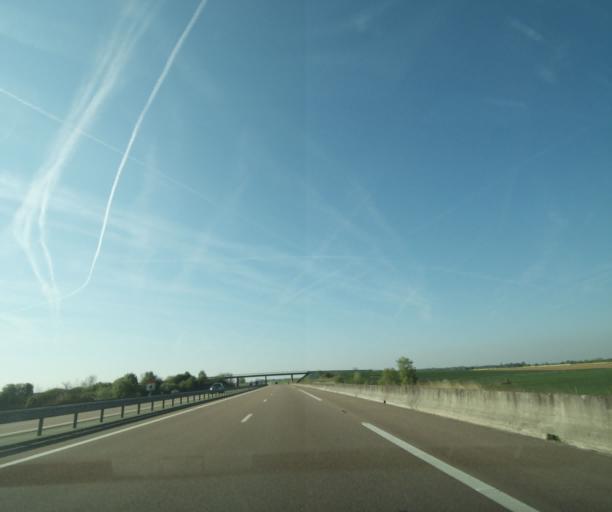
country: FR
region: Ile-de-France
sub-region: Departement de Seine-et-Marne
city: Souppes-sur-Loing
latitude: 48.1911
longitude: 2.7674
